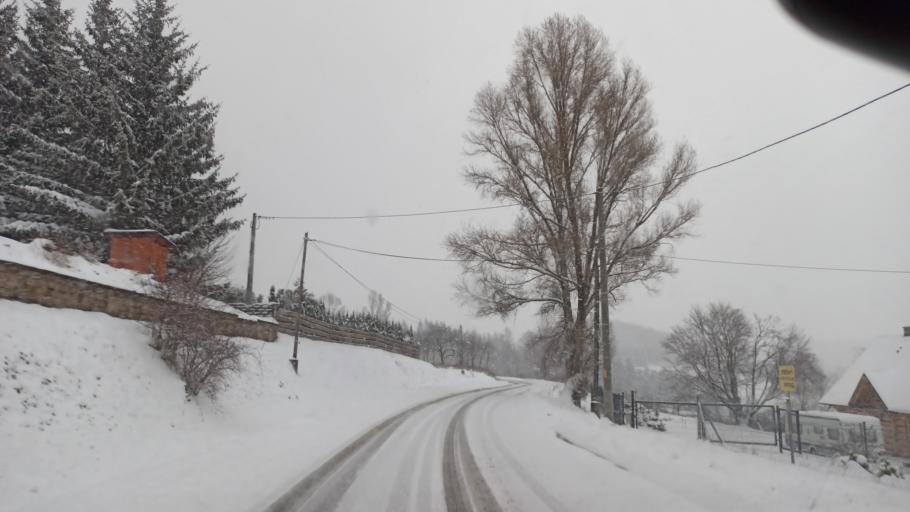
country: PL
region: Lower Silesian Voivodeship
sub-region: Powiat klodzki
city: Ludwikowice Klodzkie
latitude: 50.6499
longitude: 16.4769
